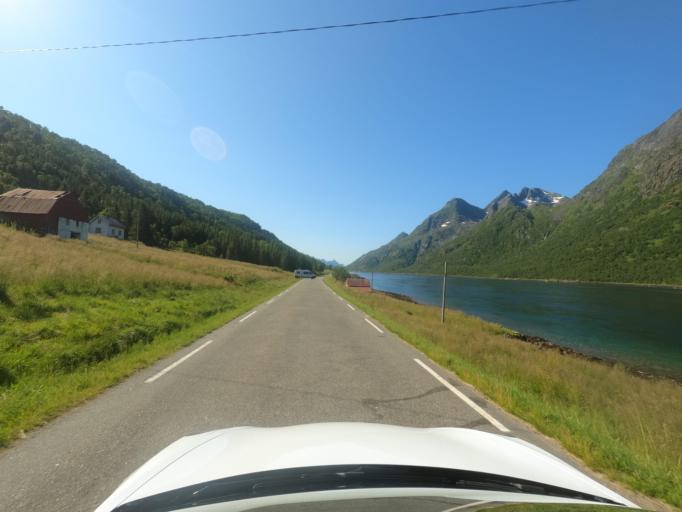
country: NO
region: Nordland
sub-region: Hadsel
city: Stokmarknes
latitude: 68.4111
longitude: 15.1296
